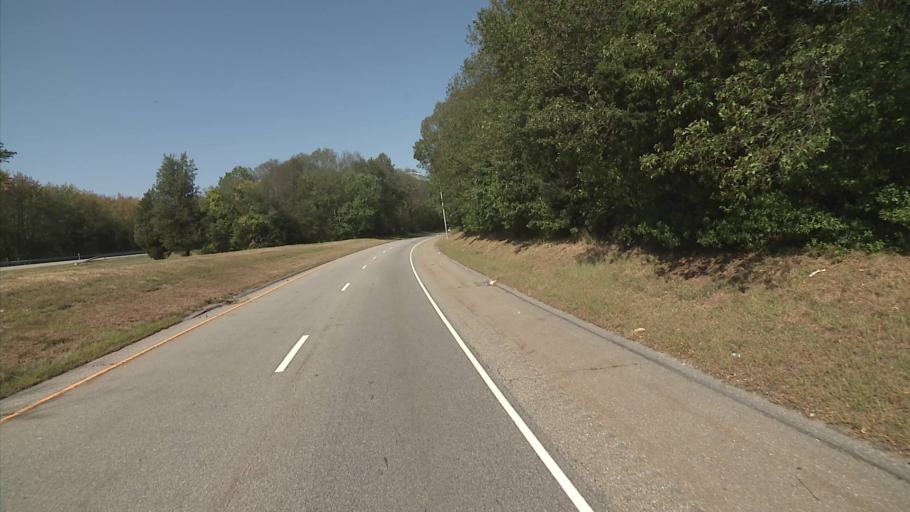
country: US
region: Connecticut
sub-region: New London County
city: Uncasville
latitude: 41.4260
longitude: -72.1218
